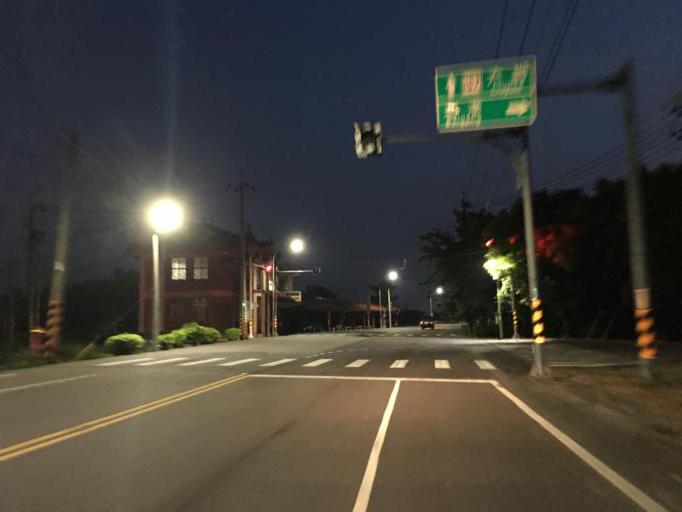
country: TW
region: Taiwan
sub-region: Chiayi
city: Taibao
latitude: 23.5248
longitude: 120.3225
